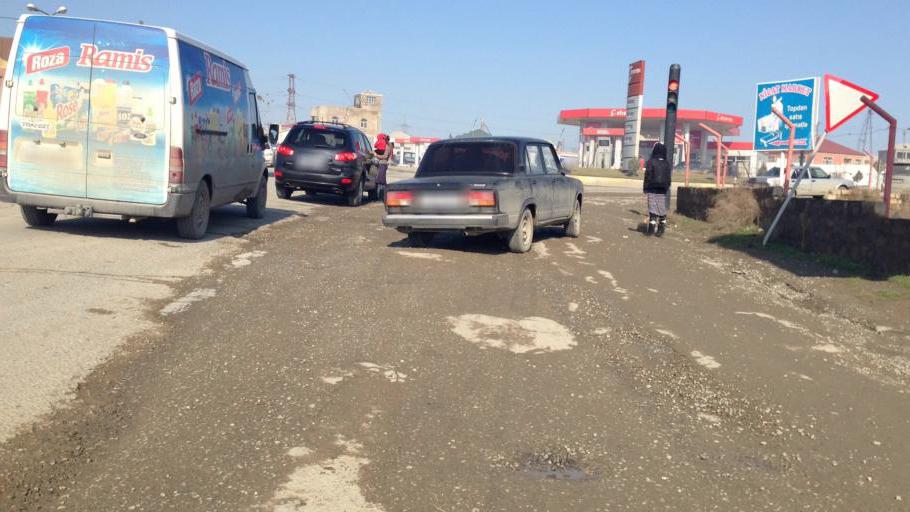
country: AZ
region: Abseron
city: Digah
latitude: 40.4800
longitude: 49.8558
